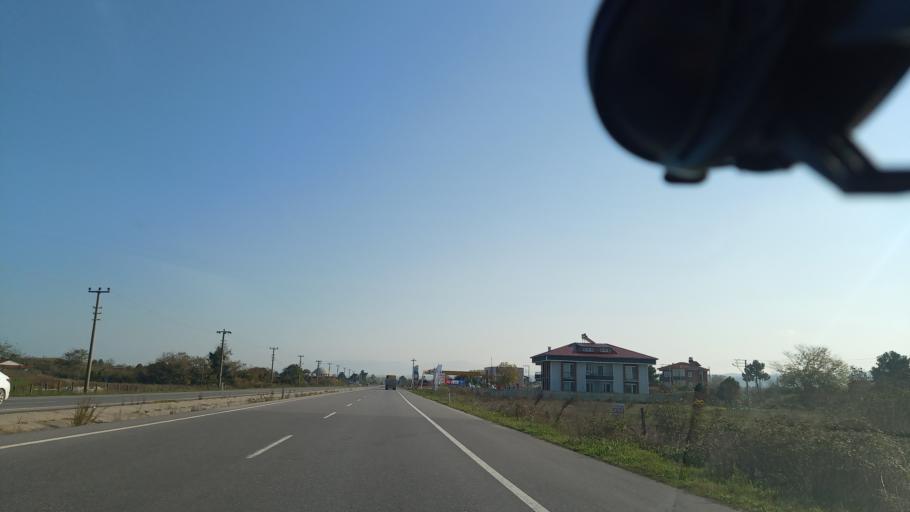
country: TR
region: Sakarya
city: Karasu
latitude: 41.0815
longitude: 30.7658
